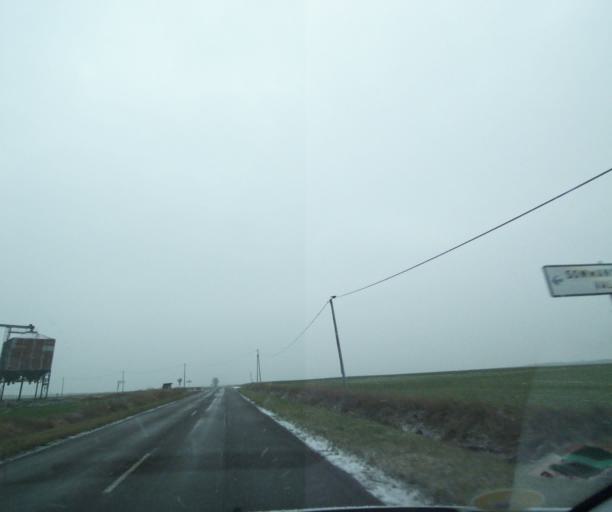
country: FR
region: Champagne-Ardenne
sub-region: Departement de la Haute-Marne
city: Wassy
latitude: 48.4851
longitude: 4.9857
